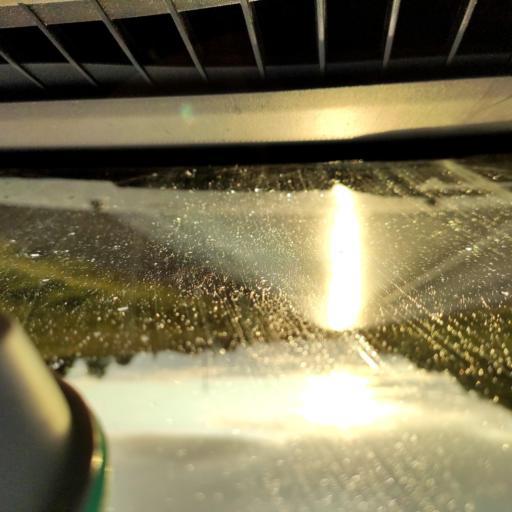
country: RU
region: Perm
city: Verkhnechusovskiye Gorodki
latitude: 58.2398
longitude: 57.0708
